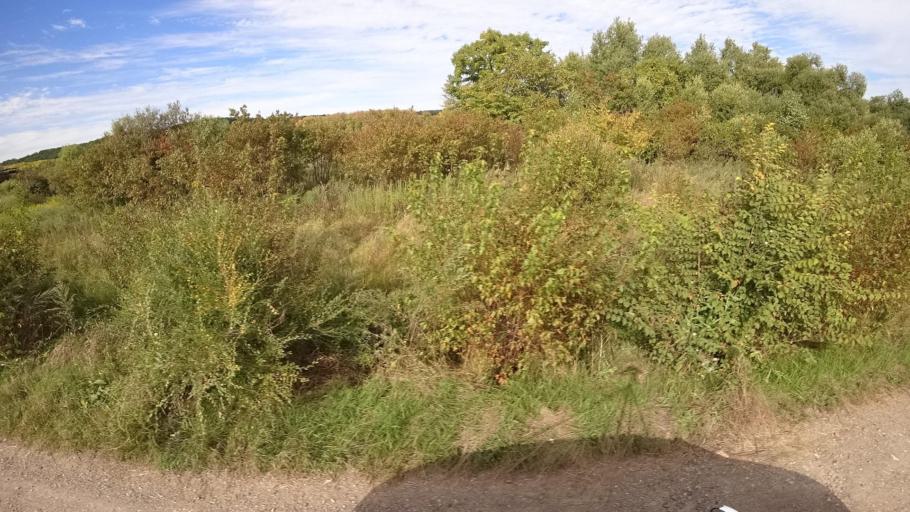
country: RU
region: Primorskiy
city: Dostoyevka
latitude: 44.3265
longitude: 133.4992
